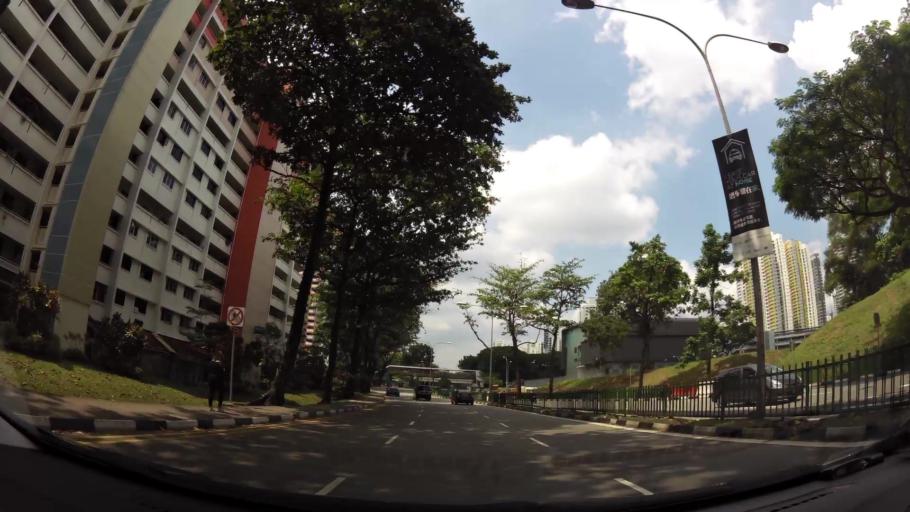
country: SG
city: Singapore
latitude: 1.2779
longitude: 103.8312
